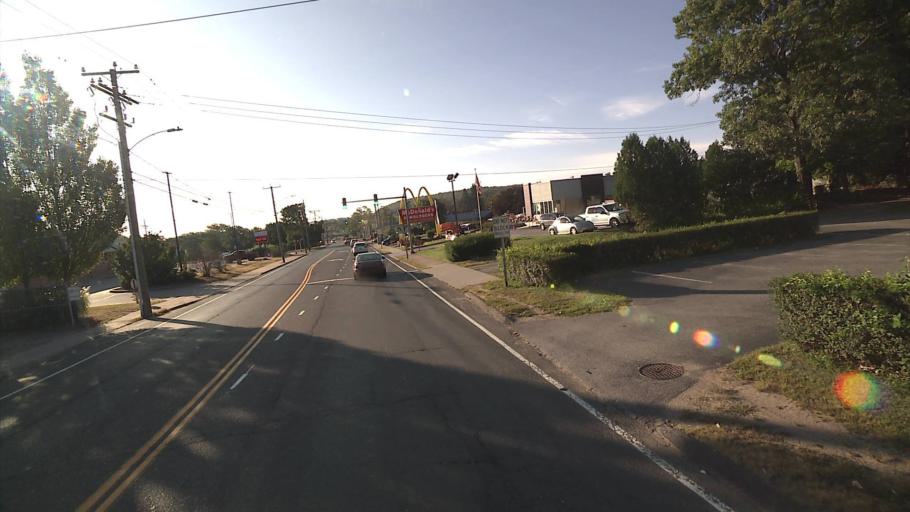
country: US
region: Connecticut
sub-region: Windham County
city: Willimantic
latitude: 41.7178
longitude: -72.2343
